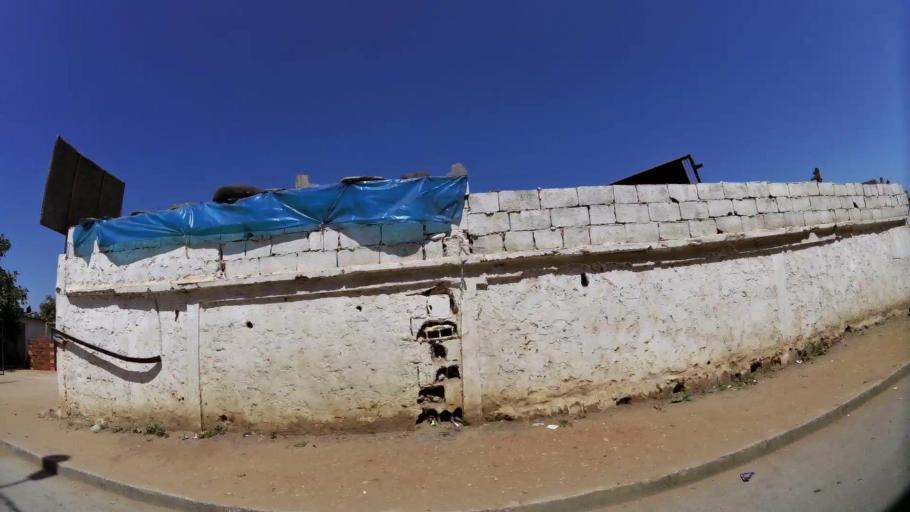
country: MA
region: Rabat-Sale-Zemmour-Zaer
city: Sale
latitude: 34.0606
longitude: -6.7780
